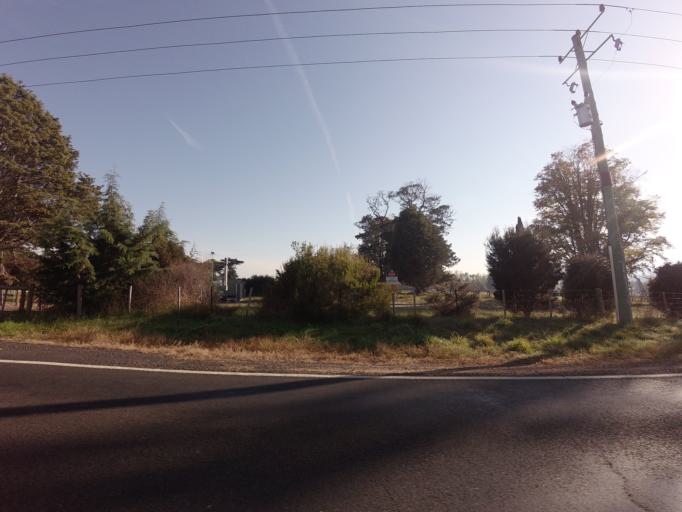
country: AU
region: Tasmania
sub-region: Launceston
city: Summerhill
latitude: -41.5266
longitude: 147.0247
